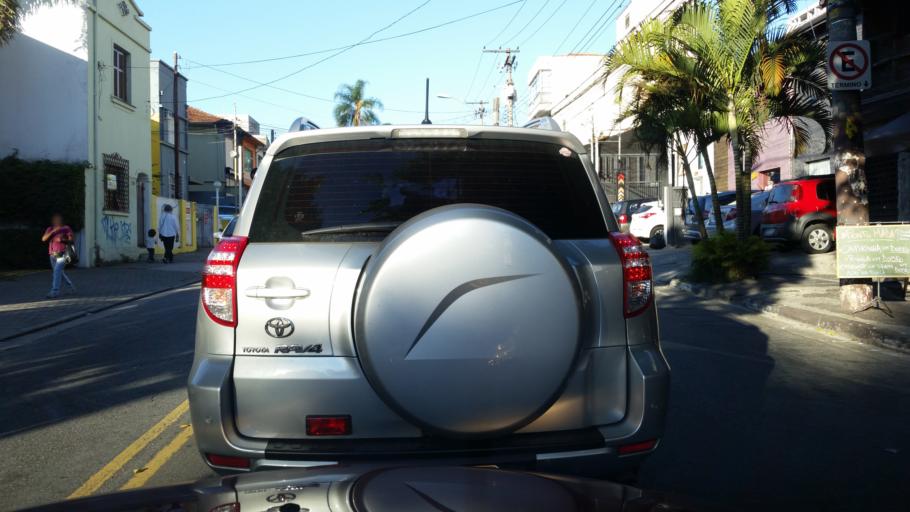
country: BR
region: Sao Paulo
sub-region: Sao Paulo
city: Sao Paulo
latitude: -23.5602
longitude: -46.6898
